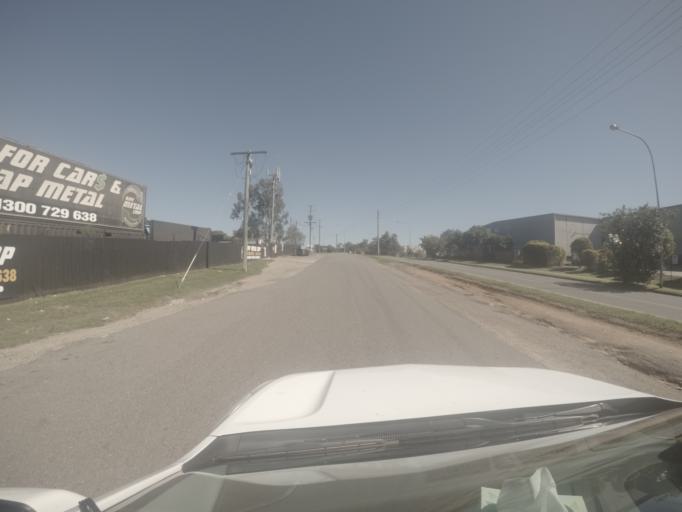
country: AU
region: Queensland
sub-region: Brisbane
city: Wacol
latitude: -27.5902
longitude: 152.9352
